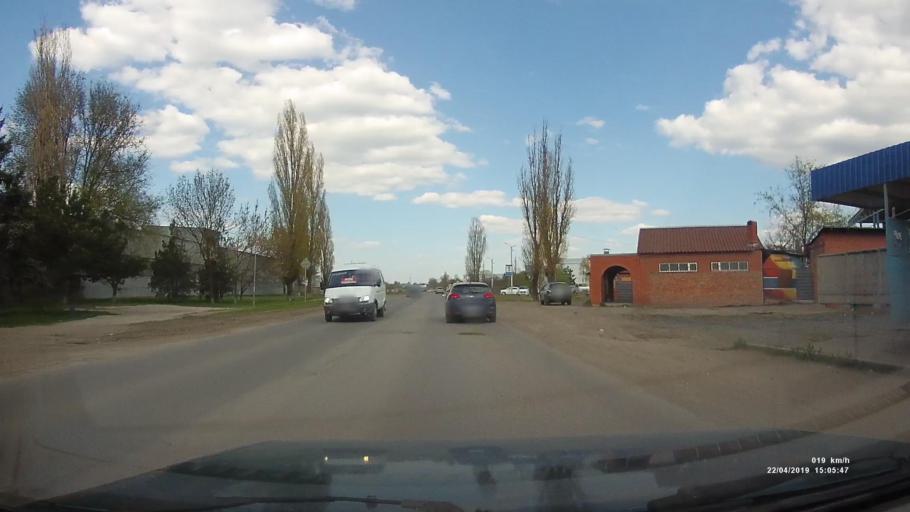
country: RU
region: Rostov
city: Azov
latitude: 47.0908
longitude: 39.3928
